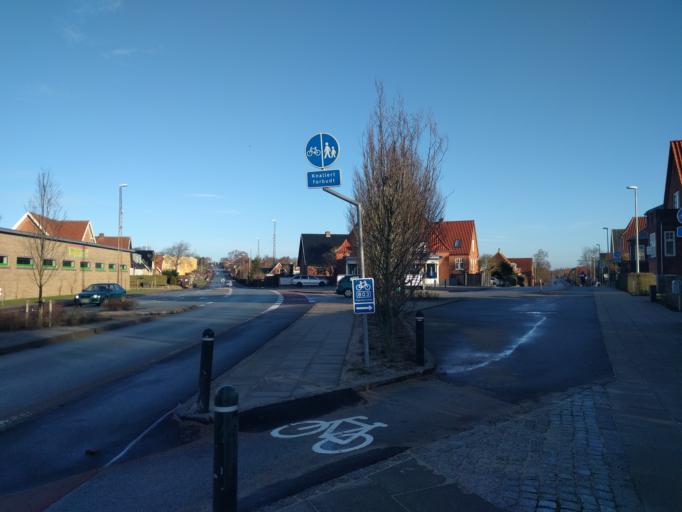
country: DK
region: Central Jutland
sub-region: Viborg Kommune
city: Viborg
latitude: 56.4599
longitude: 9.4168
